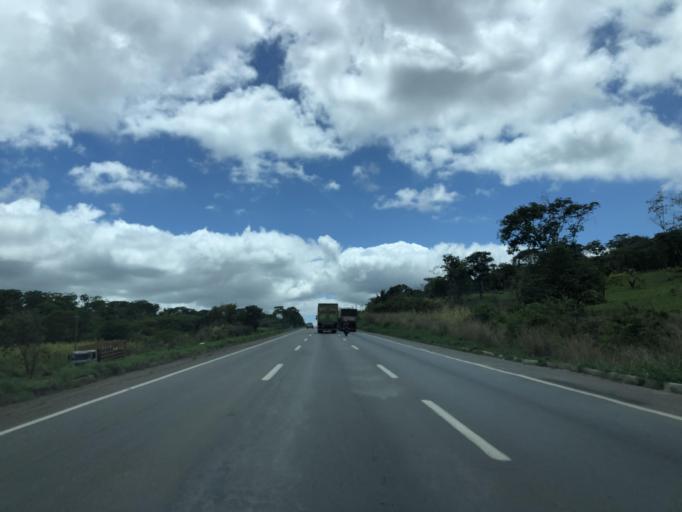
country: BR
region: Goias
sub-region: Goiania
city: Goiania
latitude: -16.5816
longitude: -49.1822
